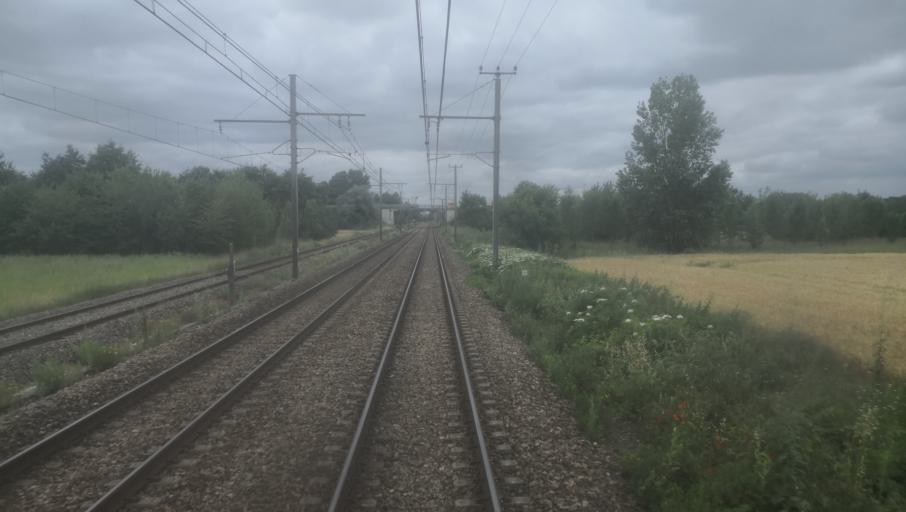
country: FR
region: Midi-Pyrenees
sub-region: Departement de la Haute-Garonne
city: Labege
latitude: 43.5340
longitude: 1.5281
